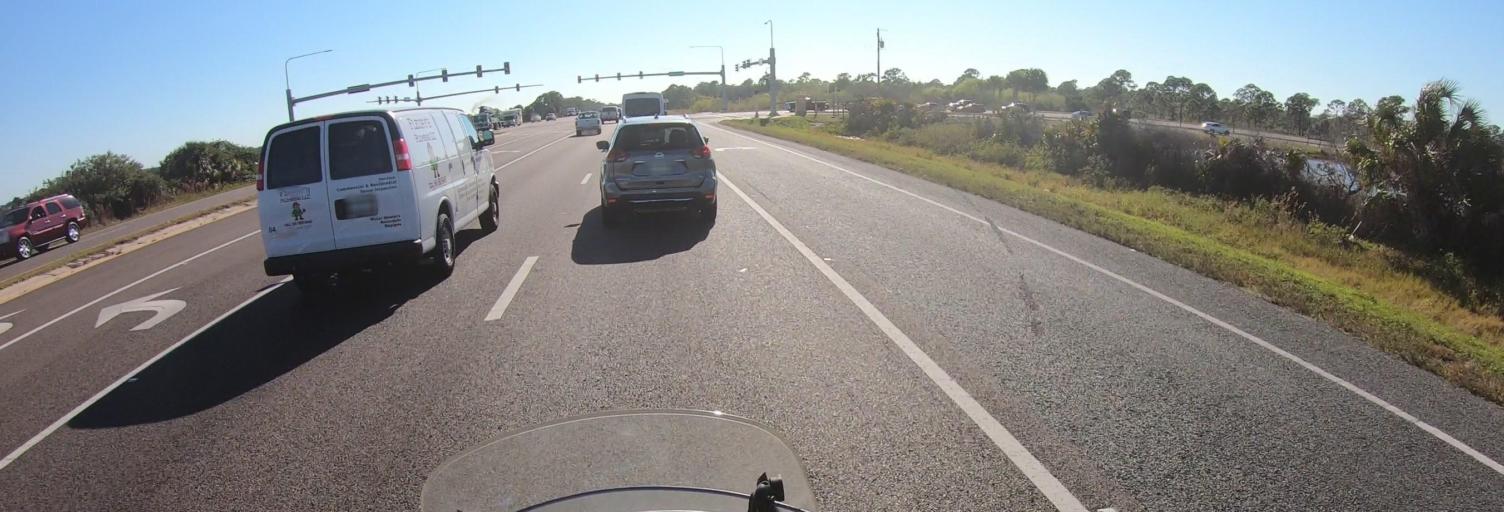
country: US
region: Florida
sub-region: Sarasota County
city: Laurel
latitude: 27.1838
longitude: -82.4438
